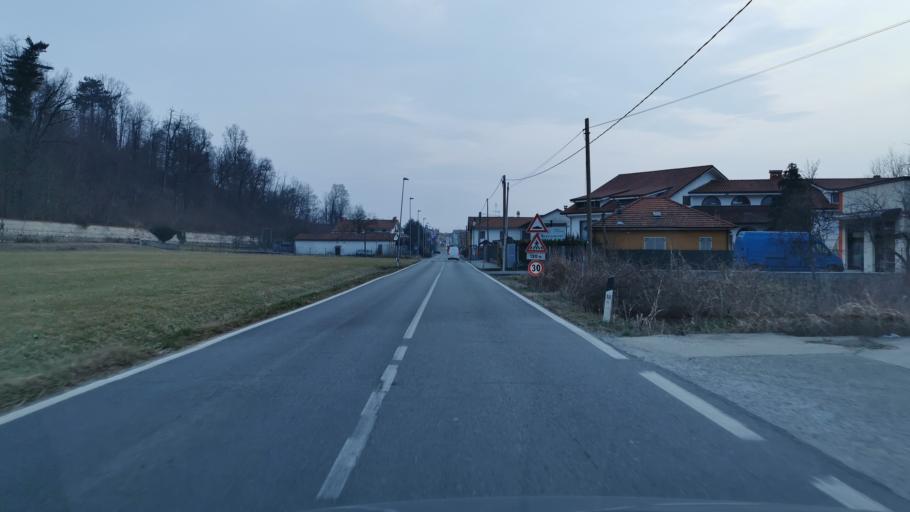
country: IT
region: Piedmont
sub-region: Provincia di Torino
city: Montalenghe
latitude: 45.3402
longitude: 7.8358
